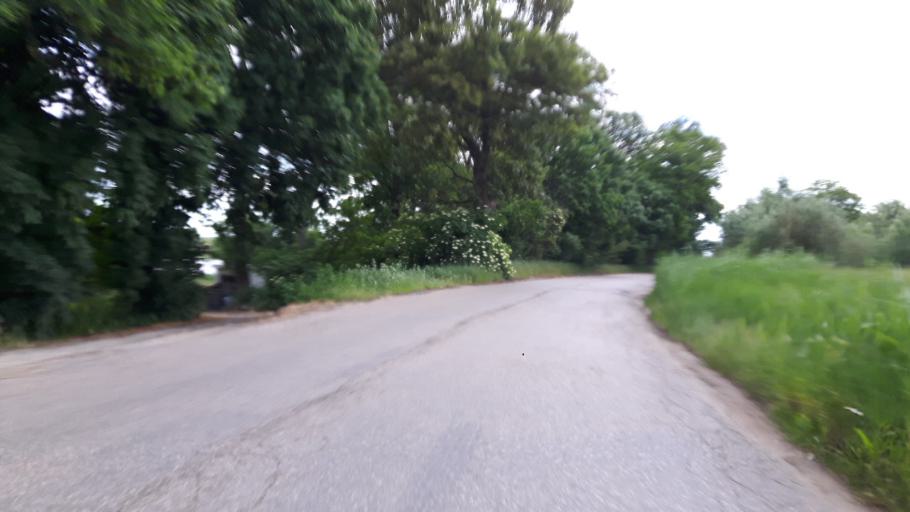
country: PL
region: Pomeranian Voivodeship
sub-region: Powiat gdanski
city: Cedry Wielkie
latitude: 54.3468
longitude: 18.7859
